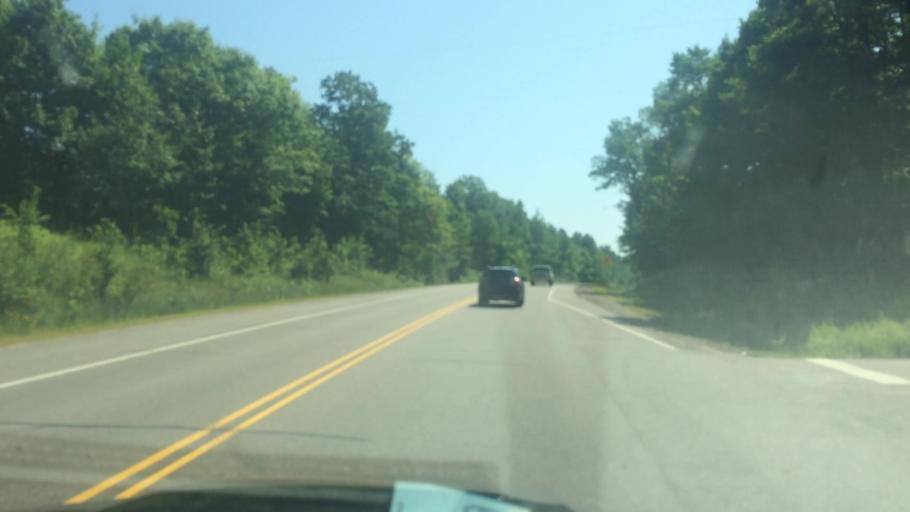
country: US
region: Wisconsin
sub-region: Oneida County
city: Rhinelander
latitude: 45.6176
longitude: -89.5219
